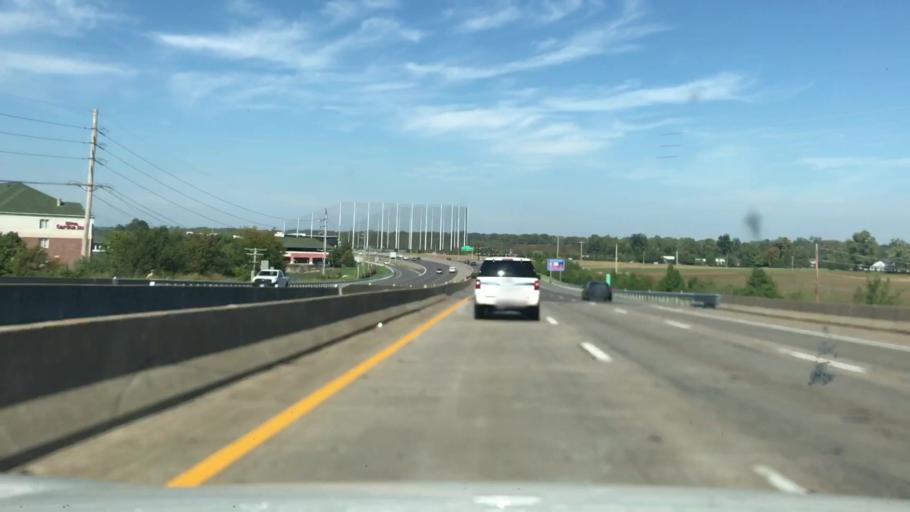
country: US
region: Missouri
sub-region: Saint Louis County
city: Chesterfield
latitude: 38.6650
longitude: -90.5731
